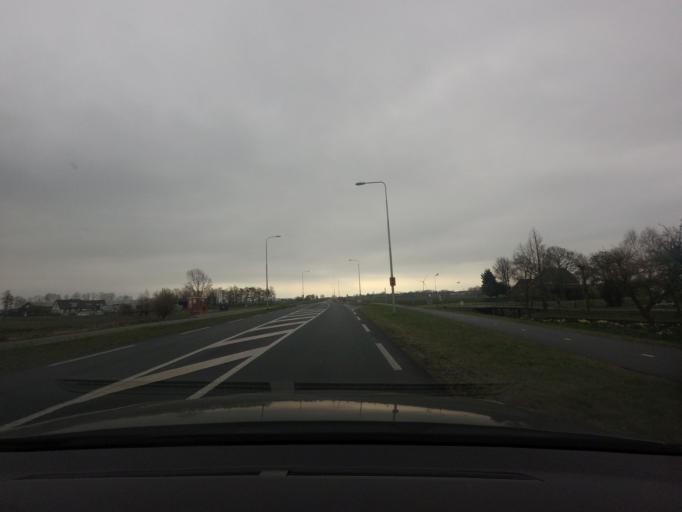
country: NL
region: Utrecht
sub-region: Gemeente De Ronde Venen
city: Mijdrecht
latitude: 52.2228
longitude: 4.8615
